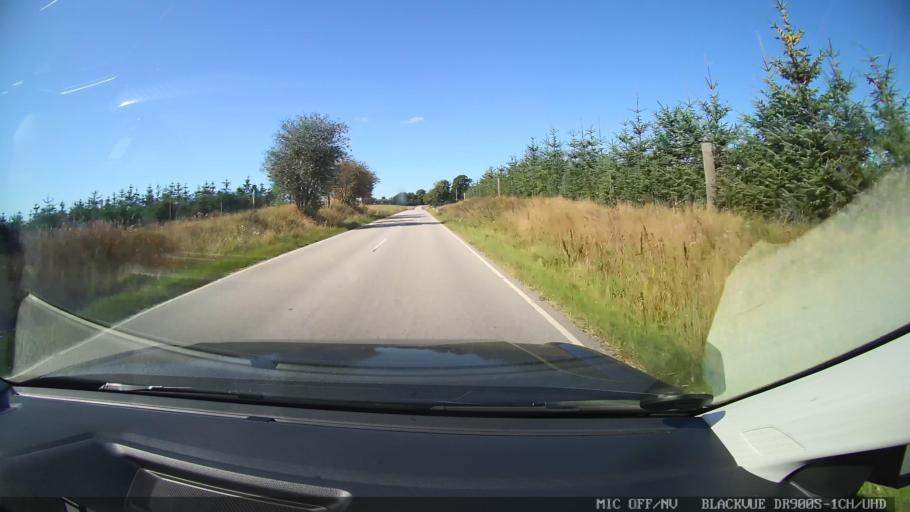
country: DK
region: North Denmark
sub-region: Mariagerfjord Kommune
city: Mariager
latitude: 56.6187
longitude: 9.9824
